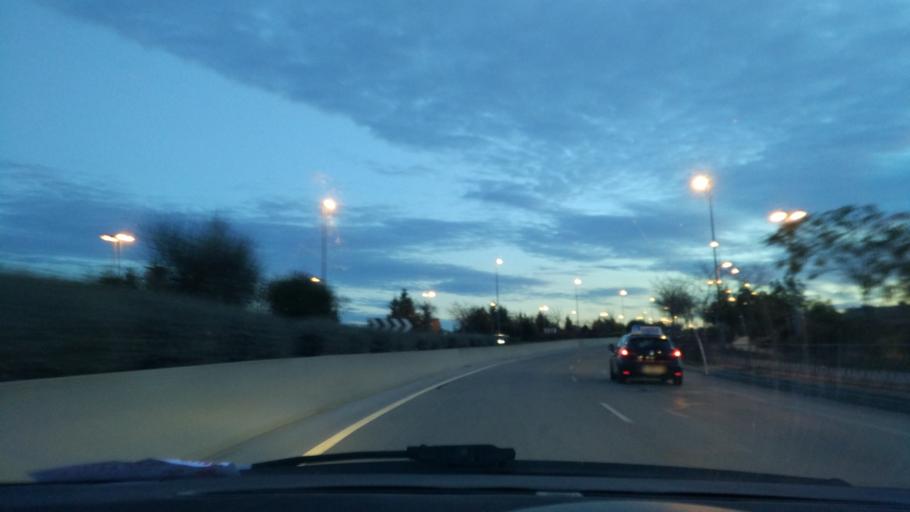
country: ES
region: Madrid
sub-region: Provincia de Madrid
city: Leganes
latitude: 40.3518
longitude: -3.7711
